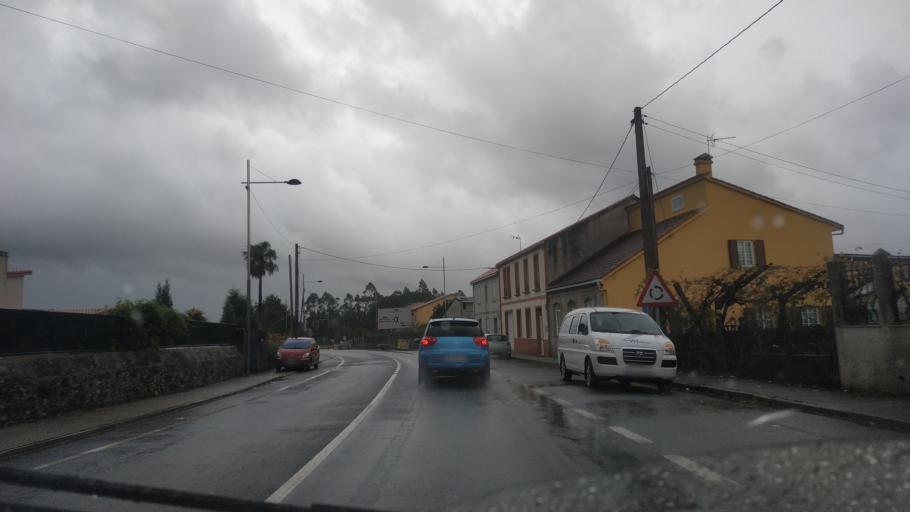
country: ES
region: Galicia
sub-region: Provincia da Coruna
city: Negreira
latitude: 42.9223
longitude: -8.7344
